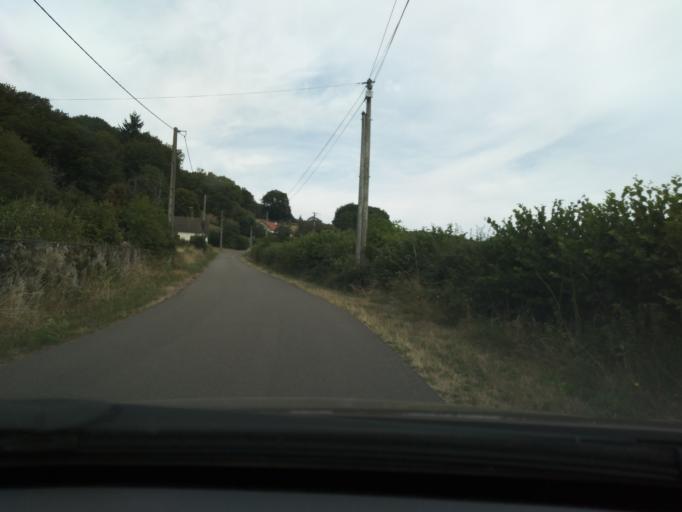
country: FR
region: Bourgogne
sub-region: Departement de la Cote-d'Or
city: Saulieu
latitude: 47.3606
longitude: 4.0929
